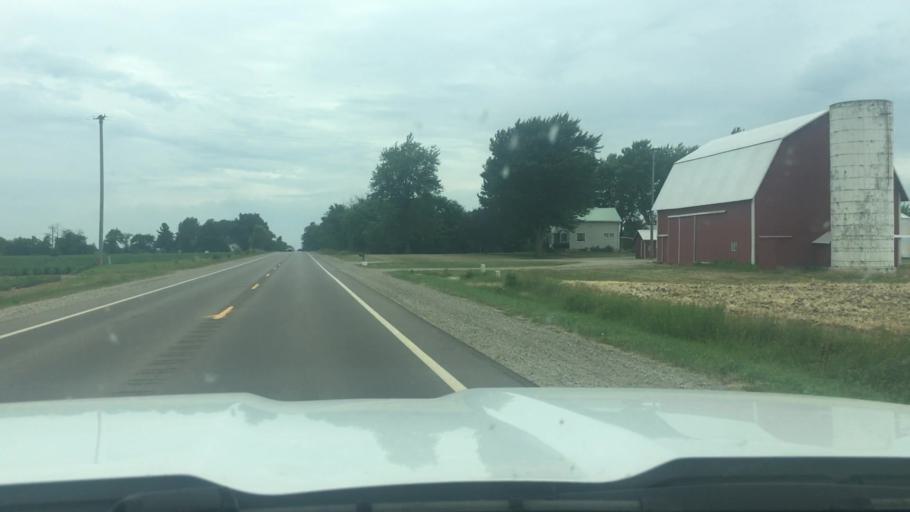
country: US
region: Michigan
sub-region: Clinton County
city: Saint Johns
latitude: 43.0020
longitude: -84.6300
